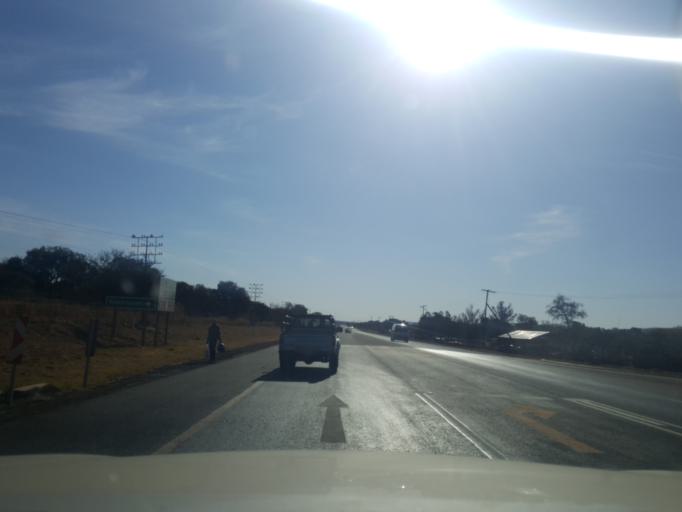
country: ZA
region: North-West
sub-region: Ngaka Modiri Molema District Municipality
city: Zeerust
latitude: -25.5270
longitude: 26.1881
